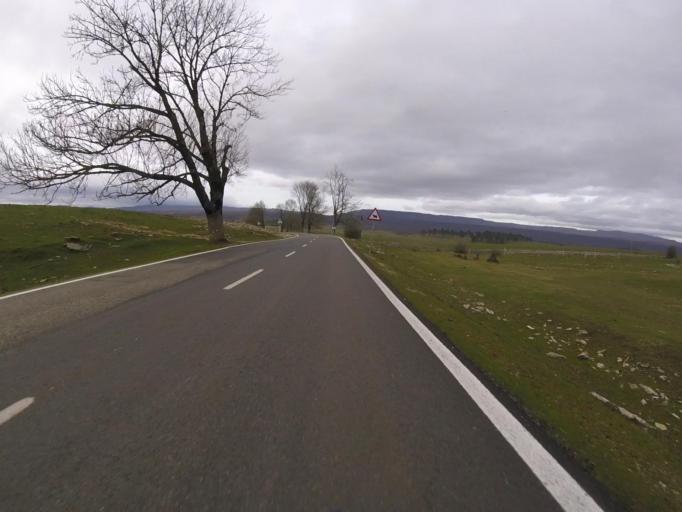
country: ES
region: Navarre
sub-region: Provincia de Navarra
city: Eulate
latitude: 42.8031
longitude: -2.1489
